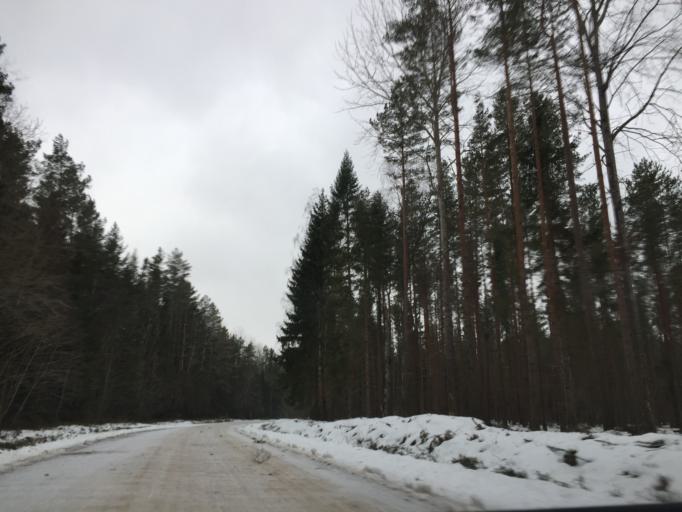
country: LV
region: Salacgrivas
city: Salacgriva
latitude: 57.6514
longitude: 24.4439
